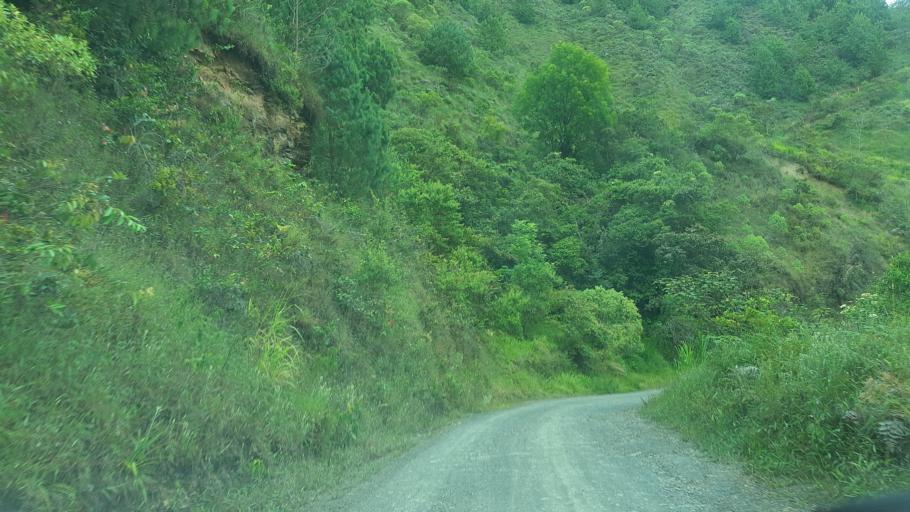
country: CO
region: Boyaca
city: Garagoa
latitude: 5.0009
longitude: -73.3327
